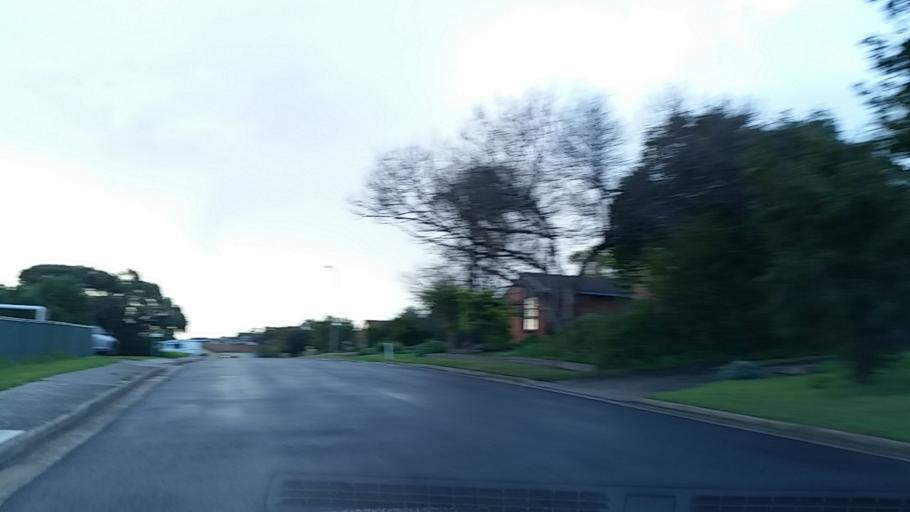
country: AU
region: South Australia
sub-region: Marion
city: Happy Valley
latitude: -35.0750
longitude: 138.5086
